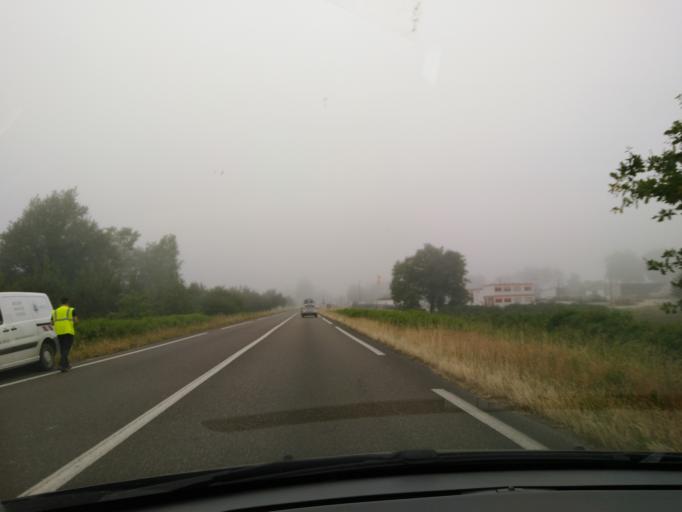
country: FR
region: Aquitaine
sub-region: Departement des Landes
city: Begaar
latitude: 43.8274
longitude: -0.8291
